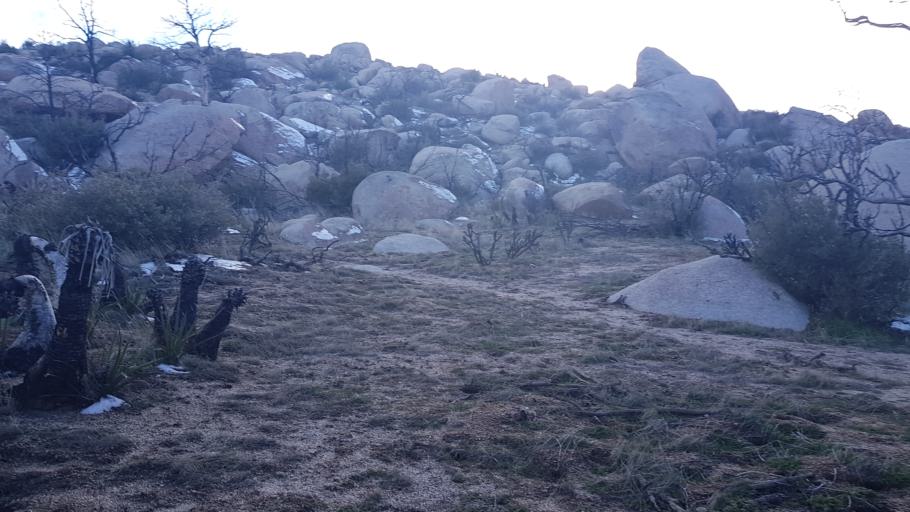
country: US
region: California
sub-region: San Diego County
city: Borrego Springs
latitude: 33.1784
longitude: -116.4324
